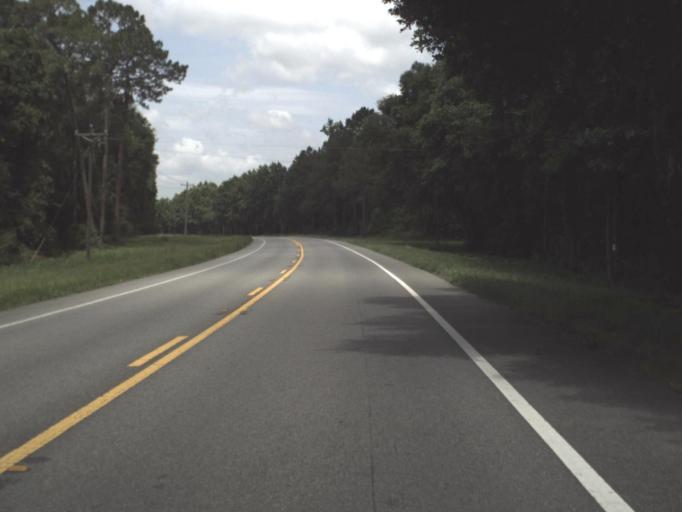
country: US
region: Florida
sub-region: Madison County
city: Madison
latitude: 30.4896
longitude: -83.5057
